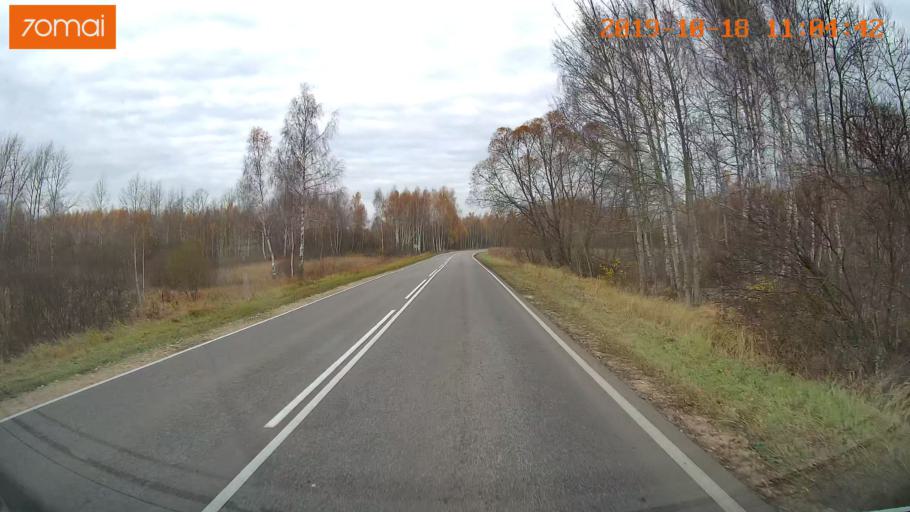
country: RU
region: Tula
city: Yepifan'
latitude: 53.8964
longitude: 38.5434
